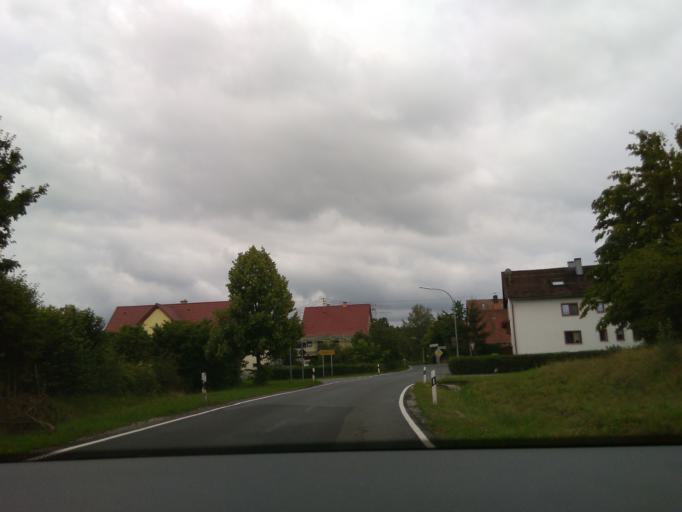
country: DE
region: Bavaria
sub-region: Regierungsbezirk Mittelfranken
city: Weisendorf
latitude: 49.6588
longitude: 10.8093
